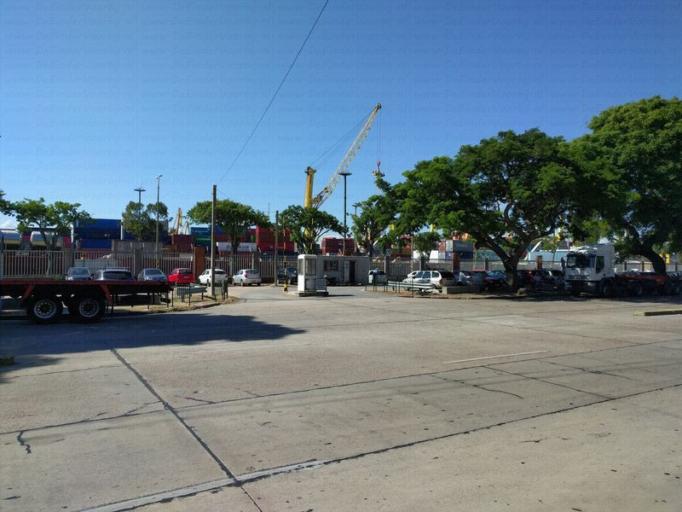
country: UY
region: Montevideo
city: Montevideo
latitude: -34.9040
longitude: -56.2074
